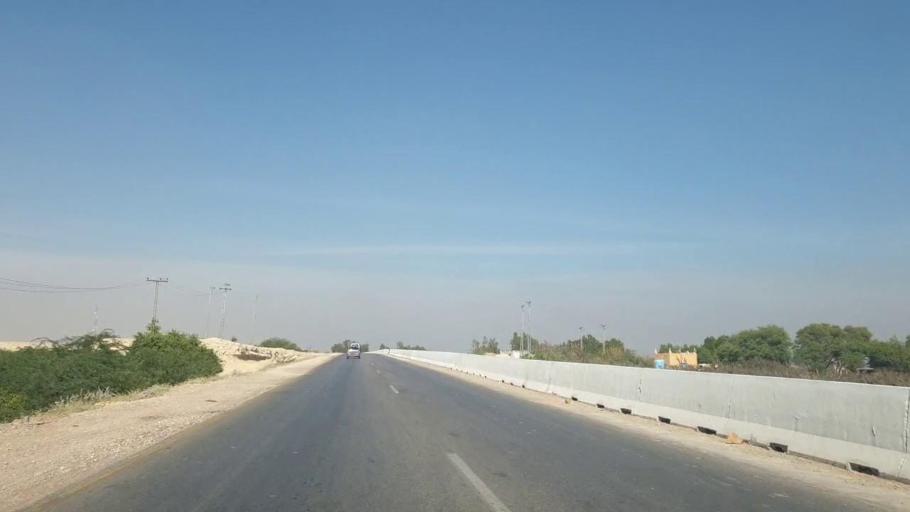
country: PK
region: Sindh
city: Hala
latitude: 25.7103
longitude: 68.2959
